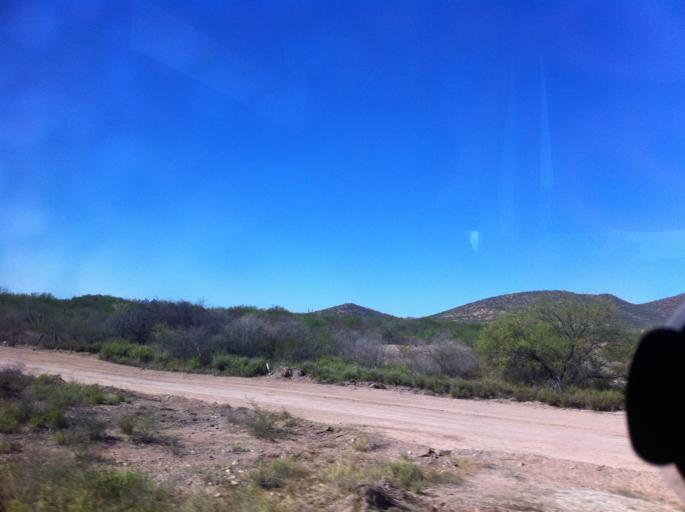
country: MX
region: Sonora
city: Heroica Guaymas
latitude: 27.9969
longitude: -110.9386
